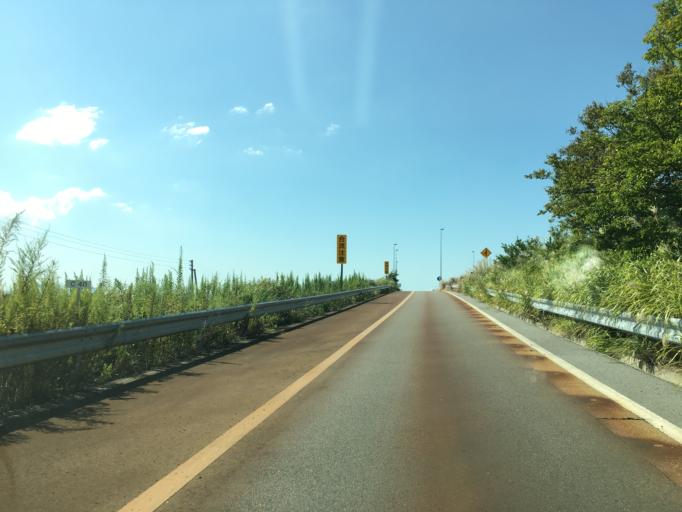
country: JP
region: Niigata
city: Niitsu-honcho
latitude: 37.8207
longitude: 139.0973
